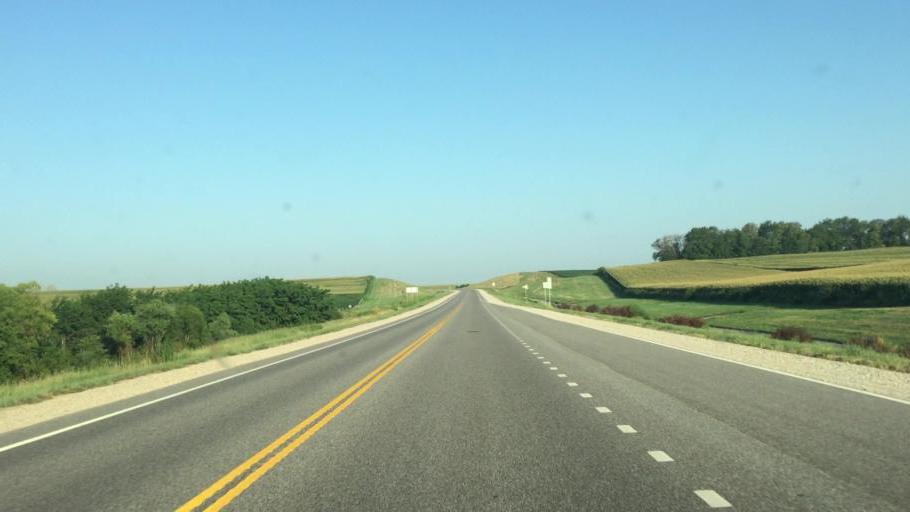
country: US
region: Kansas
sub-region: Doniphan County
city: Highland
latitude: 39.8407
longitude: -95.2704
